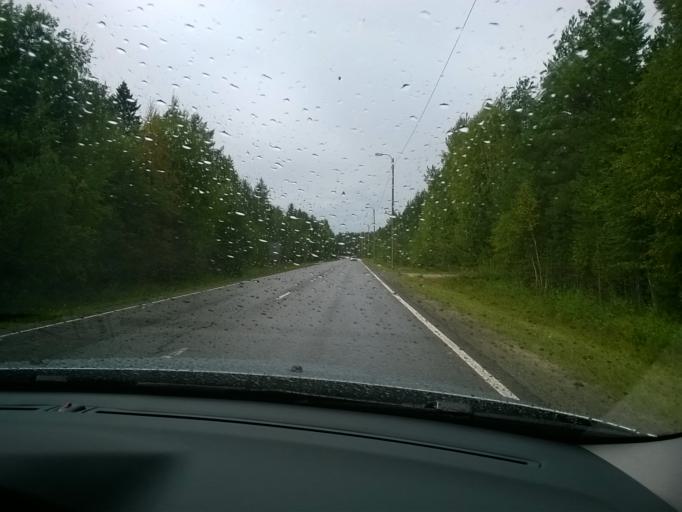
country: FI
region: Kainuu
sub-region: Kehys-Kainuu
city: Kuhmo
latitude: 64.1196
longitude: 29.5621
